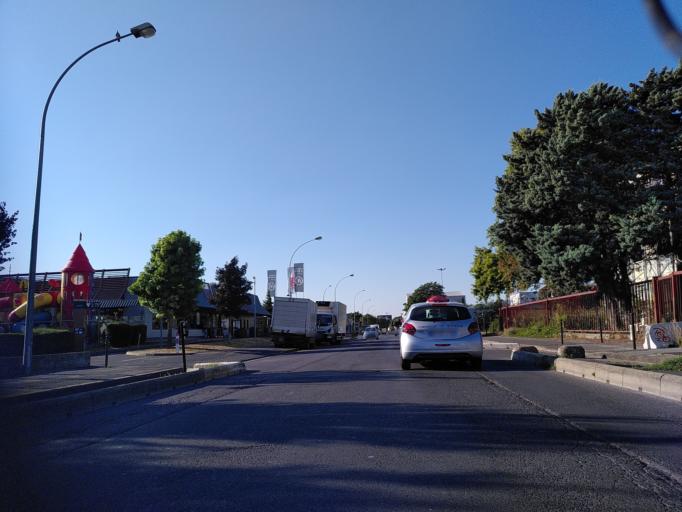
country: FR
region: Ile-de-France
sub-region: Departement du Val-de-Marne
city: Vitry-sur-Seine
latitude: 48.7950
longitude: 2.4131
